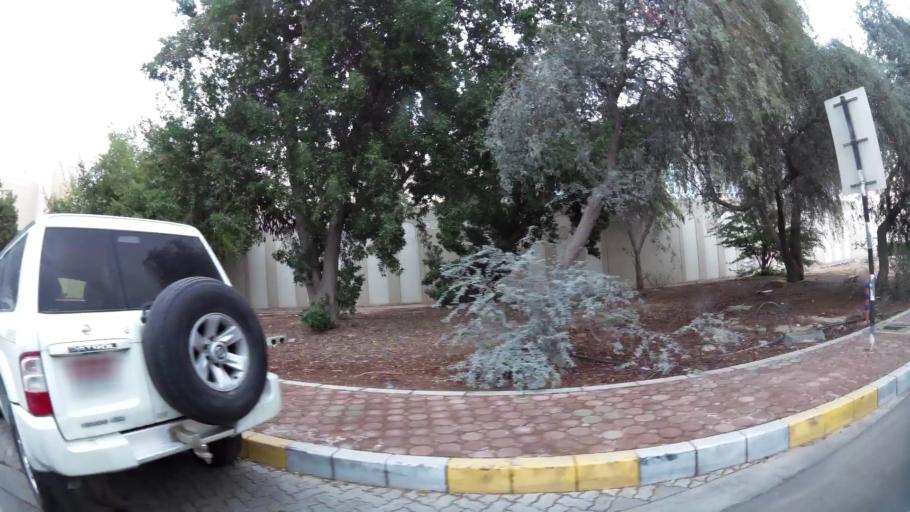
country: AE
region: Abu Dhabi
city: Abu Dhabi
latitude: 24.4311
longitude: 54.4262
